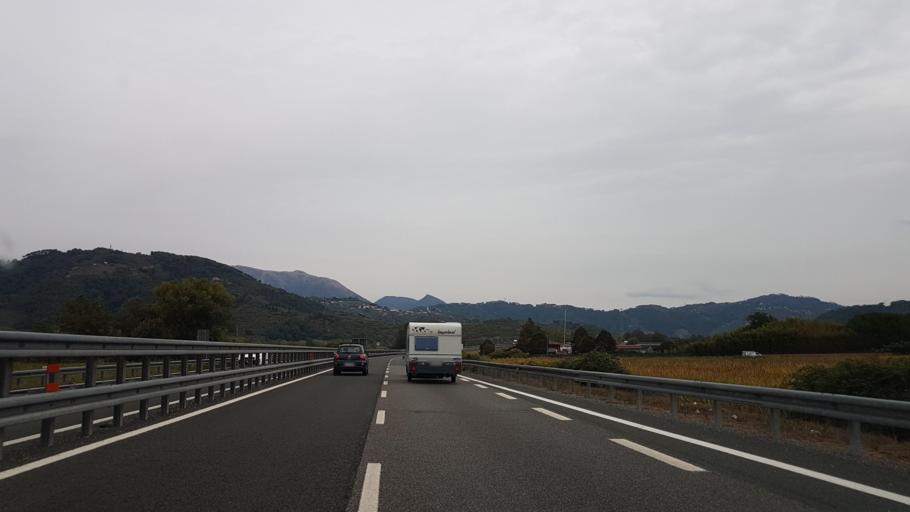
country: IT
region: Tuscany
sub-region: Provincia di Lucca
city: Piano di Mommio
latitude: 43.8913
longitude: 10.2716
